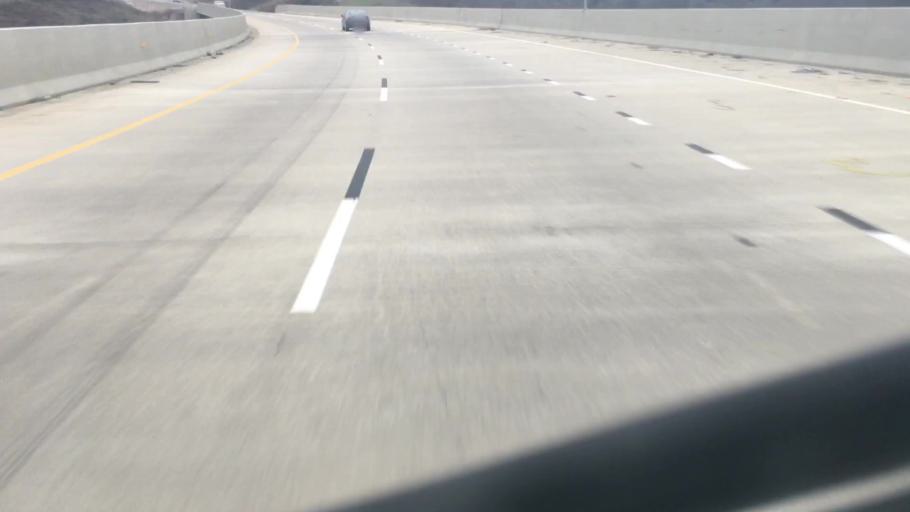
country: US
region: Alabama
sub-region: Jefferson County
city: Fultondale
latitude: 33.5750
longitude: -86.8175
